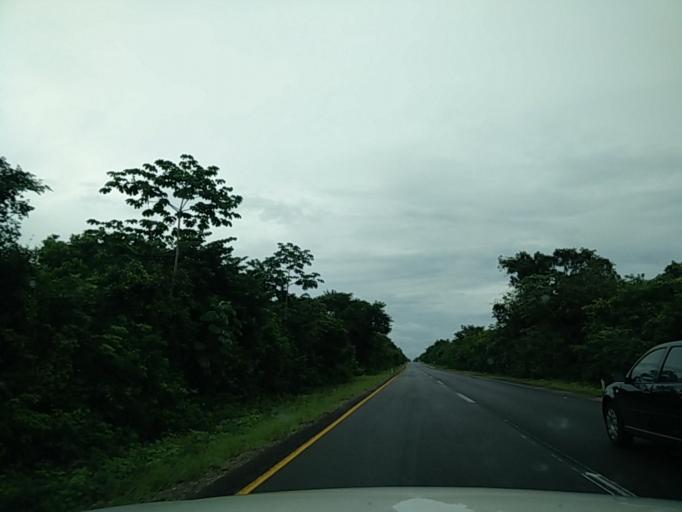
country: MX
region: Quintana Roo
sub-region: Lazaro Cardenas
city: Nuevo Xcan
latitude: 20.8842
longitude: -87.5693
